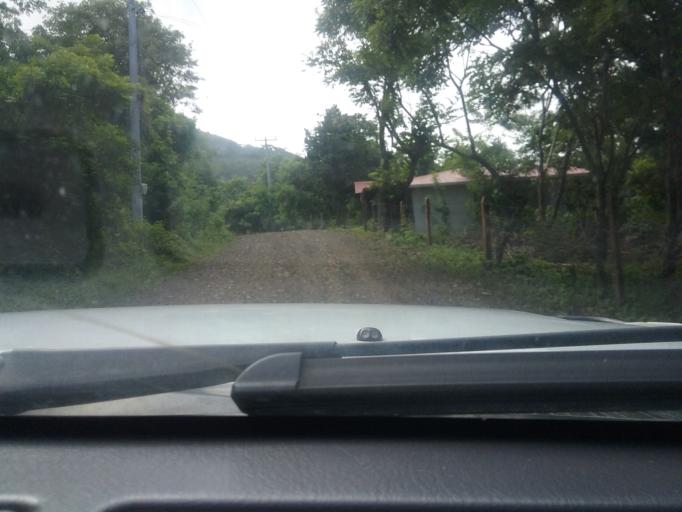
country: NI
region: Matagalpa
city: Matagalpa
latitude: 12.8814
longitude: -85.9649
